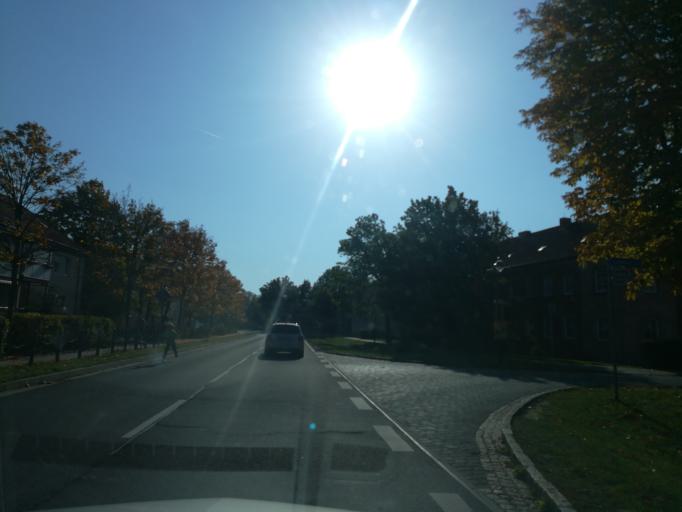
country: DE
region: Saxony-Anhalt
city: Gommern
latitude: 52.0756
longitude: 11.8231
